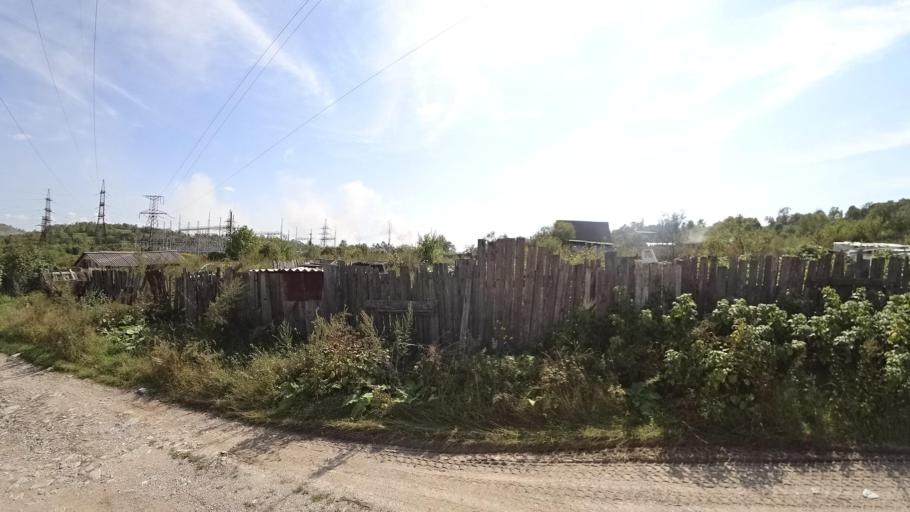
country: RU
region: Jewish Autonomous Oblast
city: Londoko
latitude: 49.0159
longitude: 131.8939
